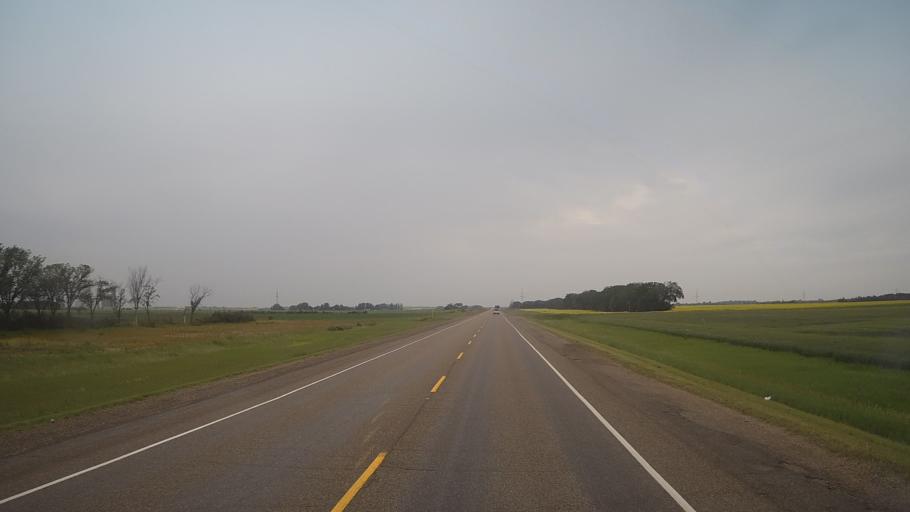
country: CA
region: Saskatchewan
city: Saskatoon
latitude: 52.1292
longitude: -106.8334
